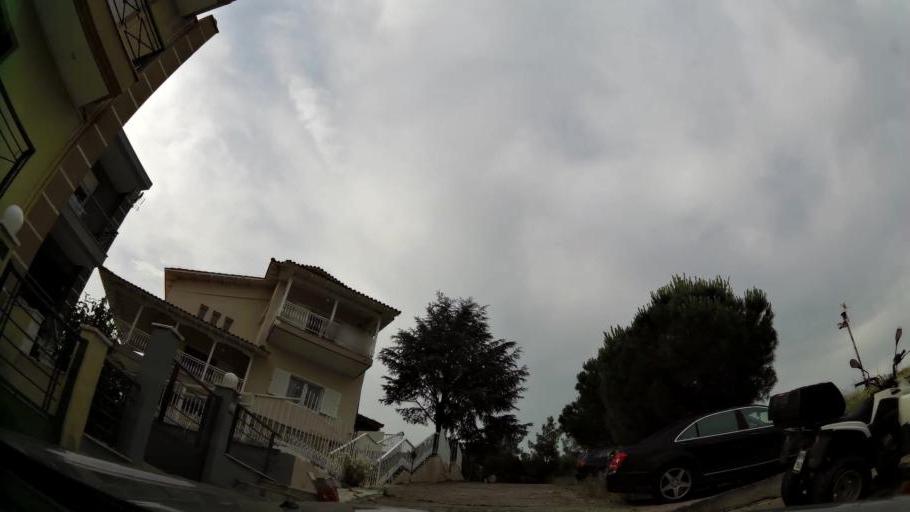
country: GR
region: Central Macedonia
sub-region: Nomos Thessalonikis
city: Oraiokastro
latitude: 40.7313
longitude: 22.9244
